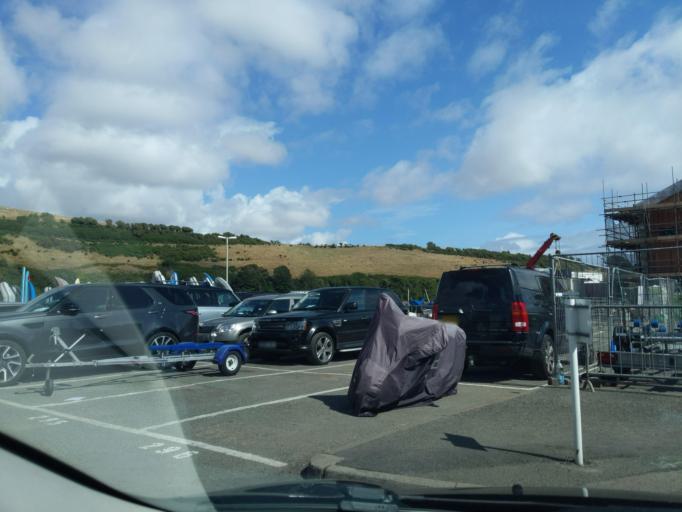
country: GB
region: England
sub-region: Devon
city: Salcombe
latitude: 50.2417
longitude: -3.7680
